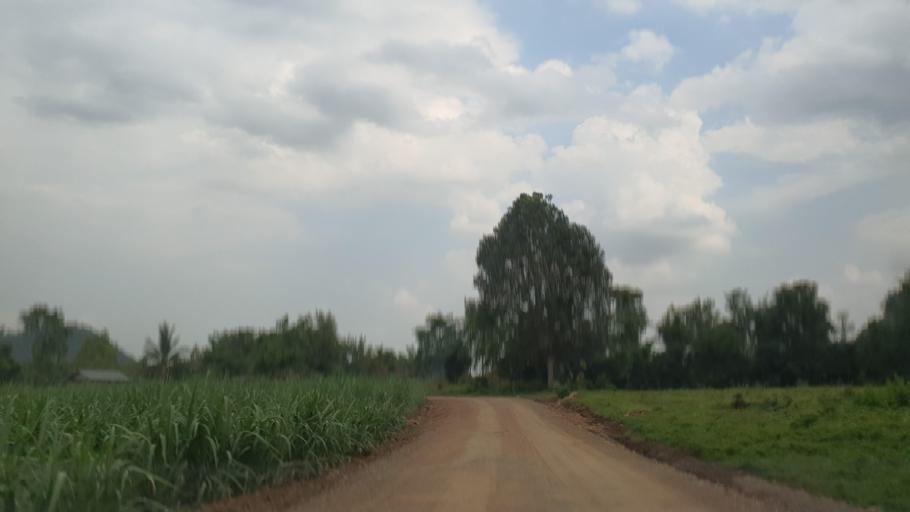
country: TH
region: Sukhothai
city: Thung Saliam
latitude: 17.2519
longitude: 99.5426
